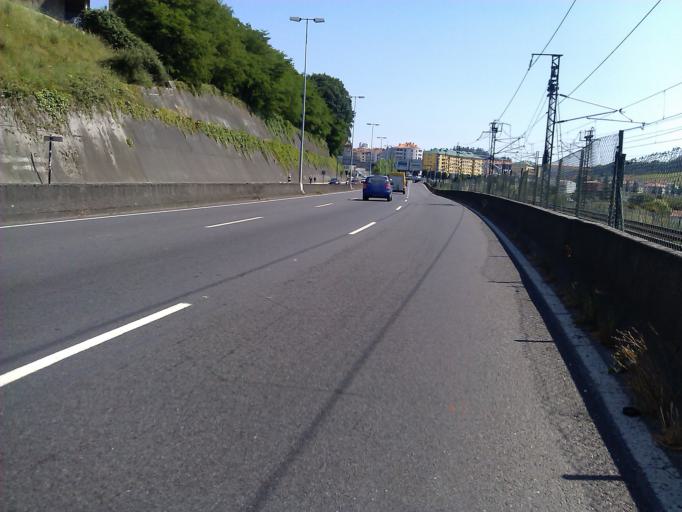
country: ES
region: Galicia
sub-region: Provincia da Coruna
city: Santiago de Compostela
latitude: 42.8746
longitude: -8.5361
